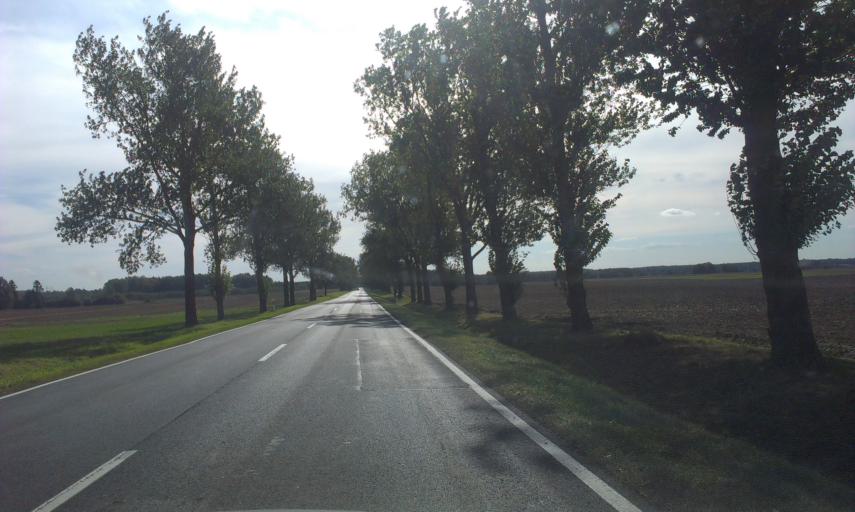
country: PL
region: Greater Poland Voivodeship
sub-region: Powiat zlotowski
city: Okonek
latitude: 53.5817
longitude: 16.8224
